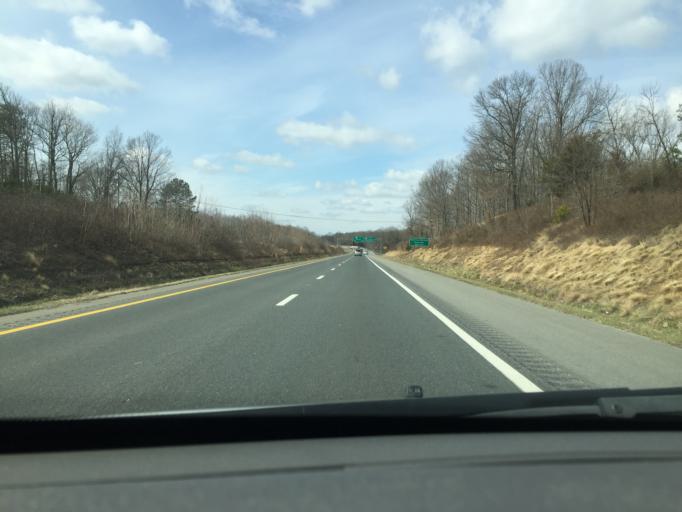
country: US
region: Virginia
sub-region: Campbell County
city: Timberlake
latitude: 37.3107
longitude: -79.2549
